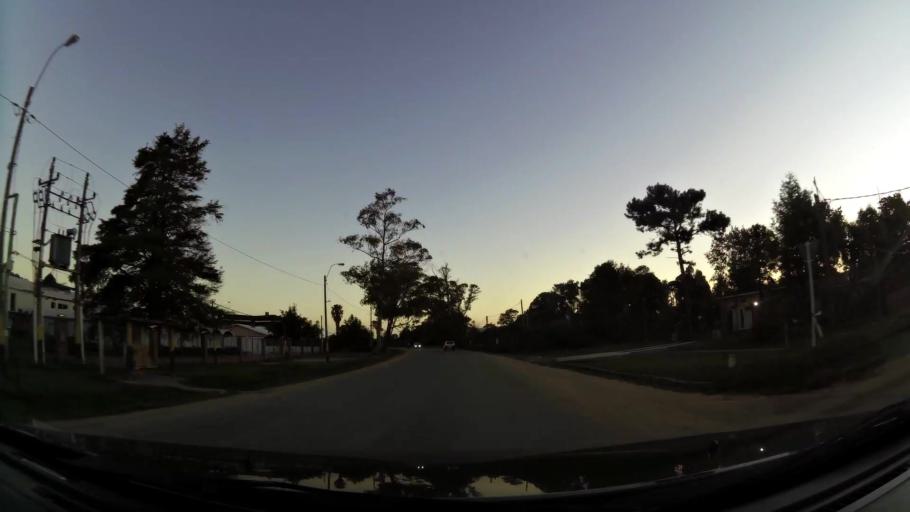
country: UY
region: Canelones
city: Barra de Carrasco
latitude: -34.8275
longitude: -55.9564
